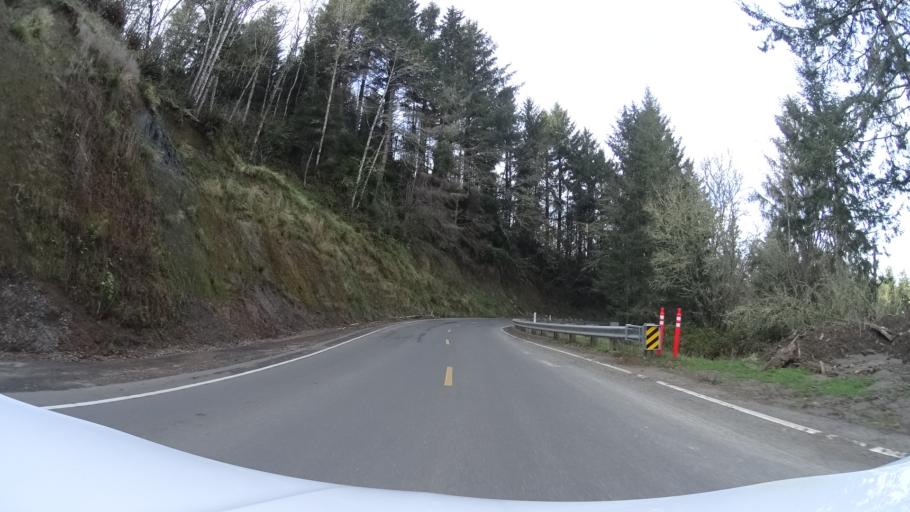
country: US
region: California
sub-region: Humboldt County
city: Ferndale
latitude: 40.5620
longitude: -124.2732
